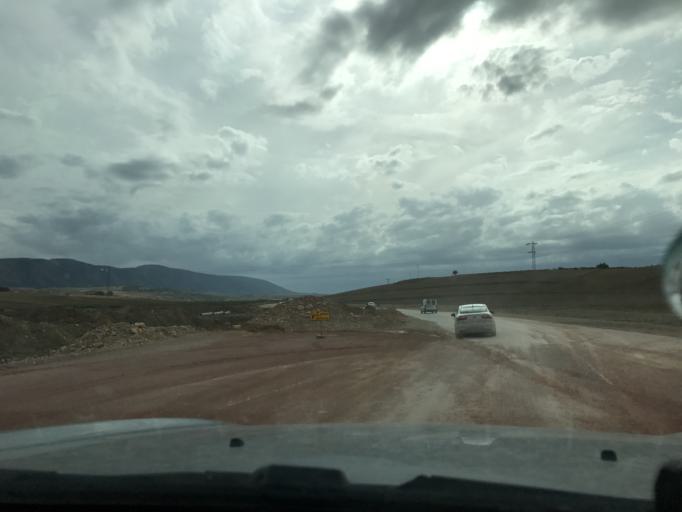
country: TN
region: Silyanah
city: Bu `Aradah
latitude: 36.1577
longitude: 9.6392
